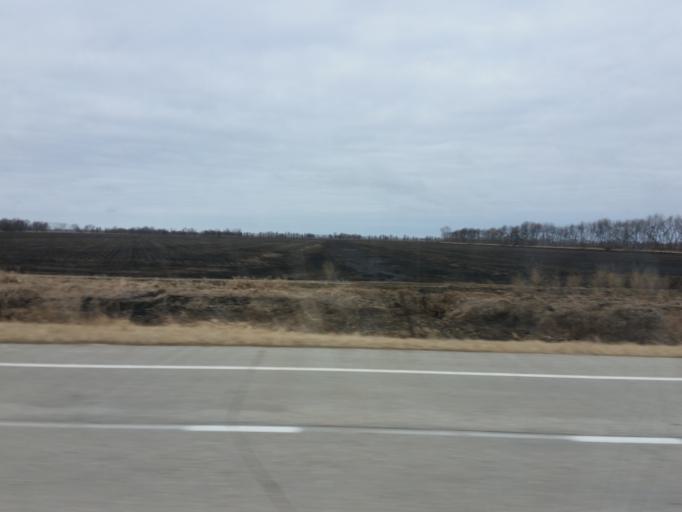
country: US
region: North Dakota
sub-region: Walsh County
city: Grafton
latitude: 48.2326
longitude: -97.1895
